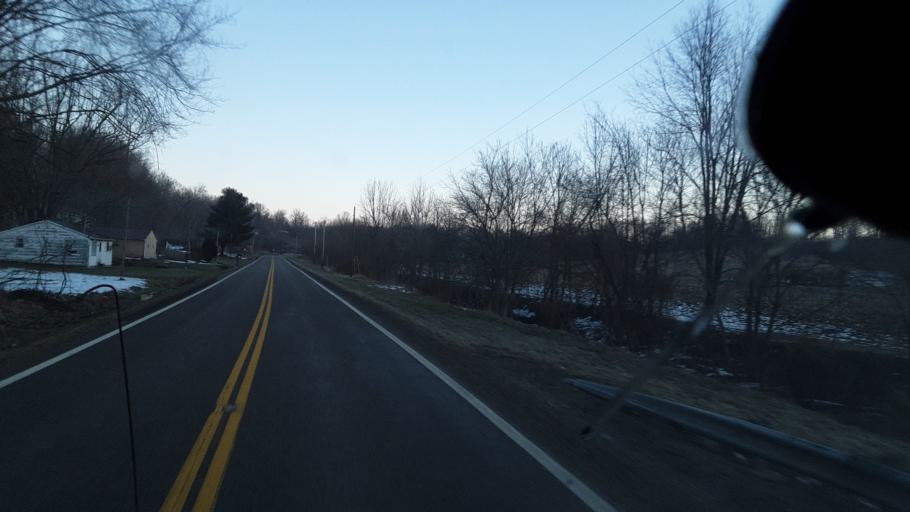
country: US
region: Ohio
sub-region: Perry County
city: Somerset
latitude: 39.7283
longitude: -82.3119
